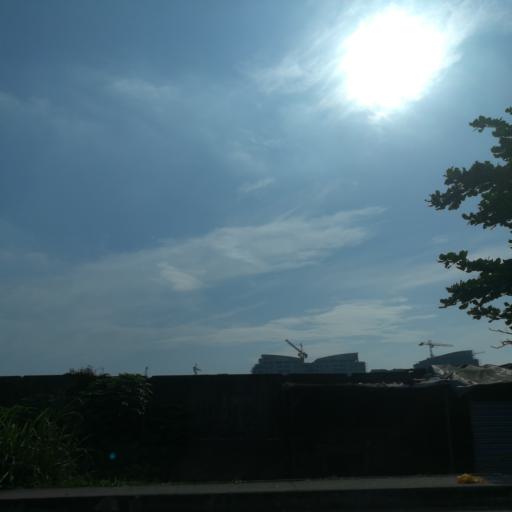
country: NG
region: Rivers
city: Port Harcourt
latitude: 4.8026
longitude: 7.0243
